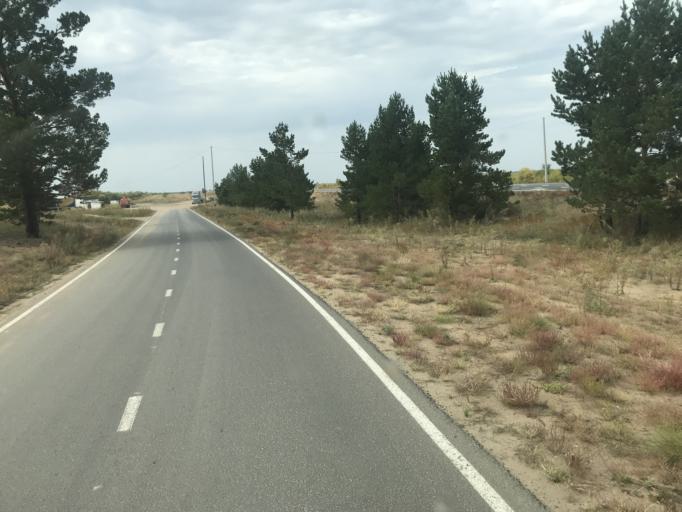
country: KZ
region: Pavlodar
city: Kurchatov
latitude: 51.3494
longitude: 78.3713
